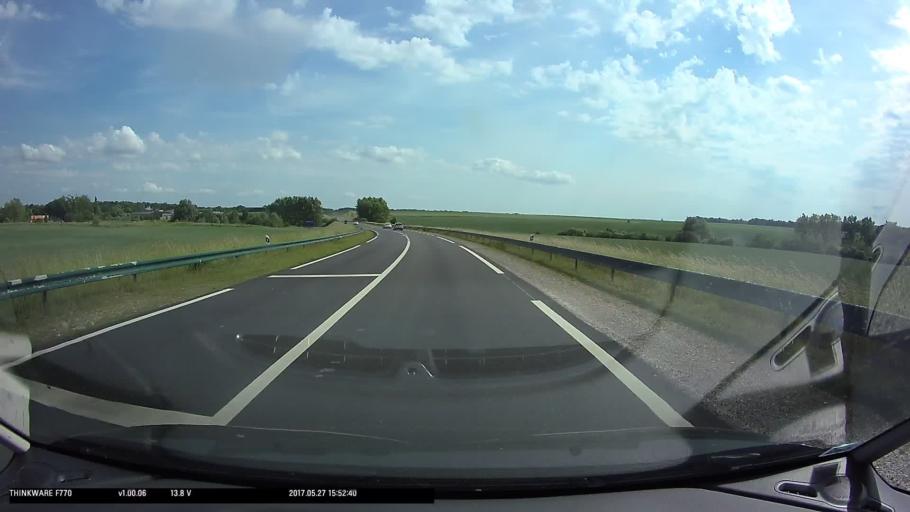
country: FR
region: Ile-de-France
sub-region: Departement du Val-d'Oise
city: Marines
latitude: 49.1494
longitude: 1.9637
